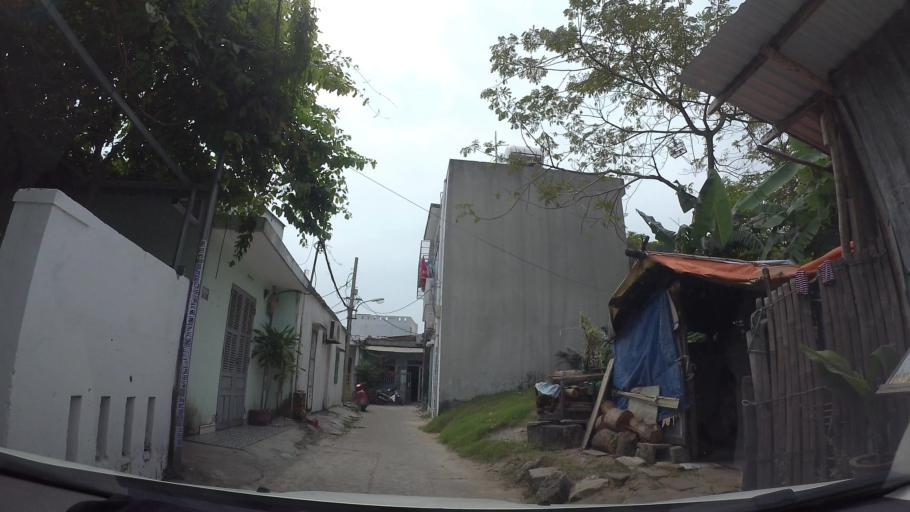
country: VN
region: Da Nang
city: Son Tra
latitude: 16.0966
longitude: 108.2480
